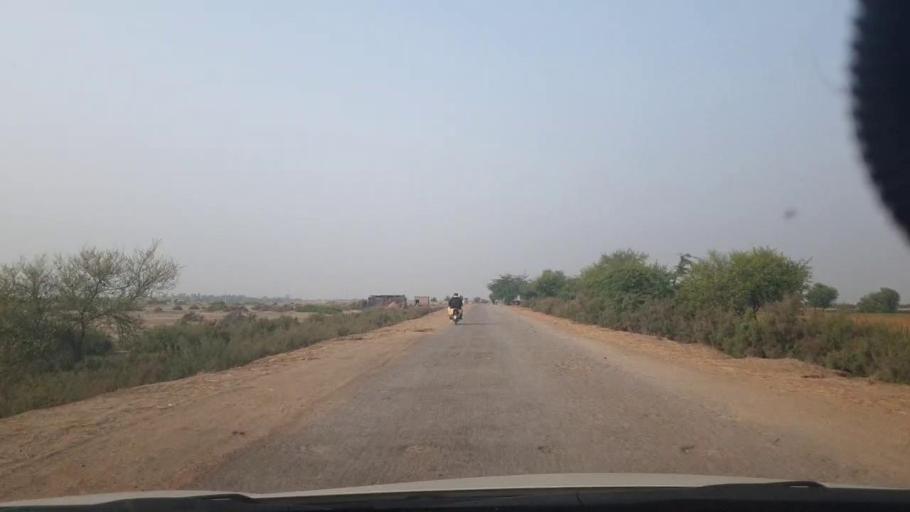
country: PK
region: Sindh
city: Bulri
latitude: 24.7836
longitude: 68.4195
